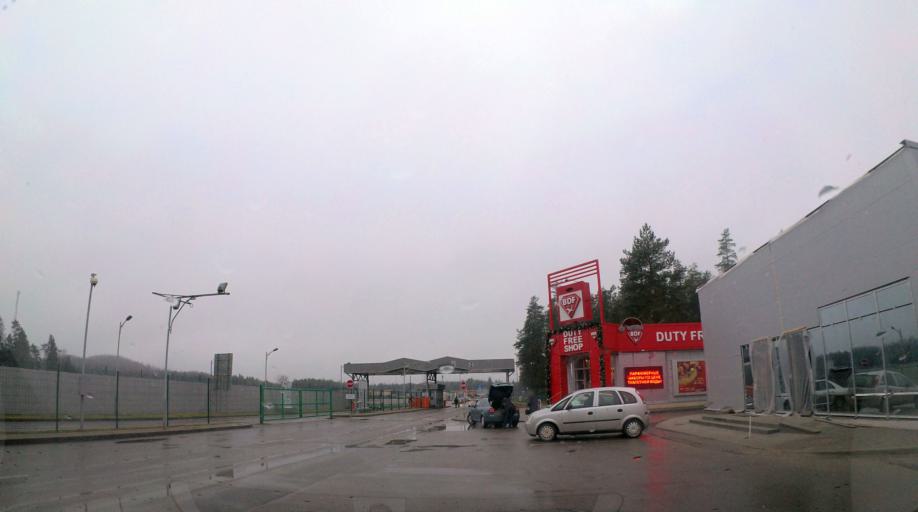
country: BY
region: Grodnenskaya
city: Astravyets
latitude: 54.7195
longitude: 25.7464
